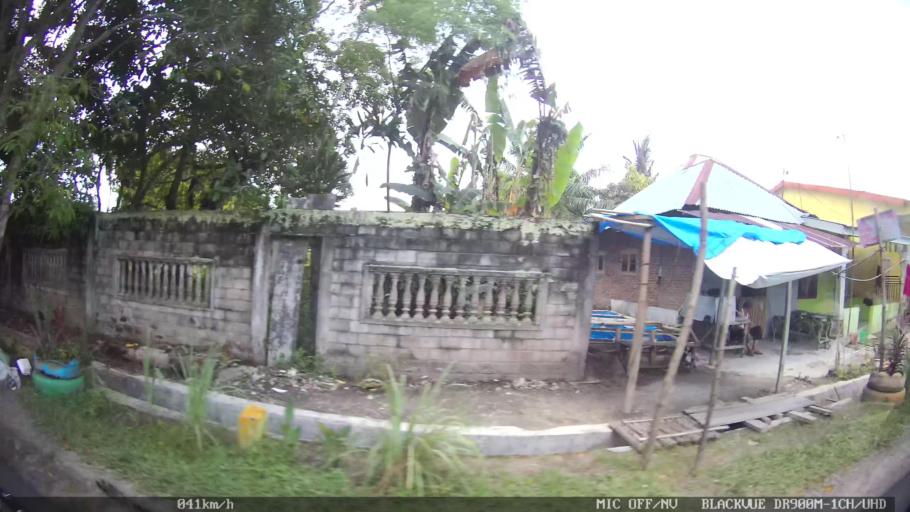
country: ID
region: North Sumatra
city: Percut
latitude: 3.5523
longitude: 98.8714
